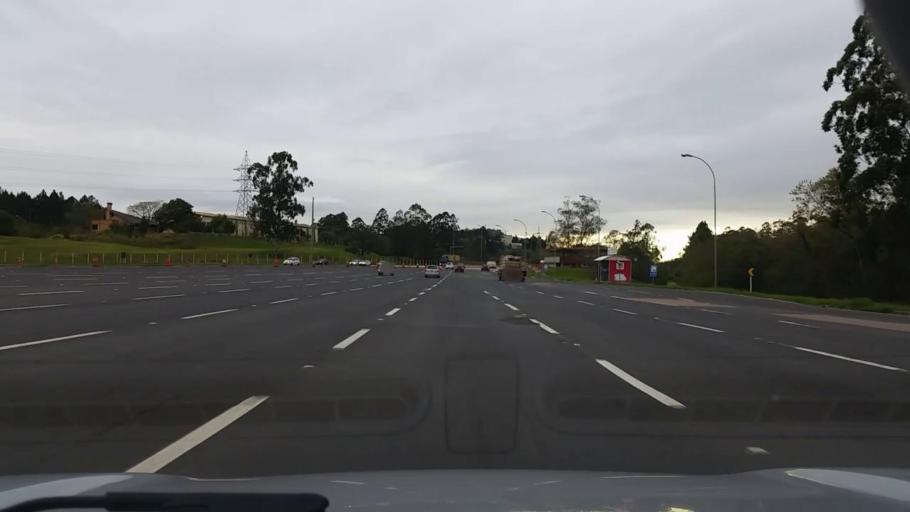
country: BR
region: Rio Grande do Sul
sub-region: Gravatai
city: Gravatai
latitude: -29.9554
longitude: -51.0307
